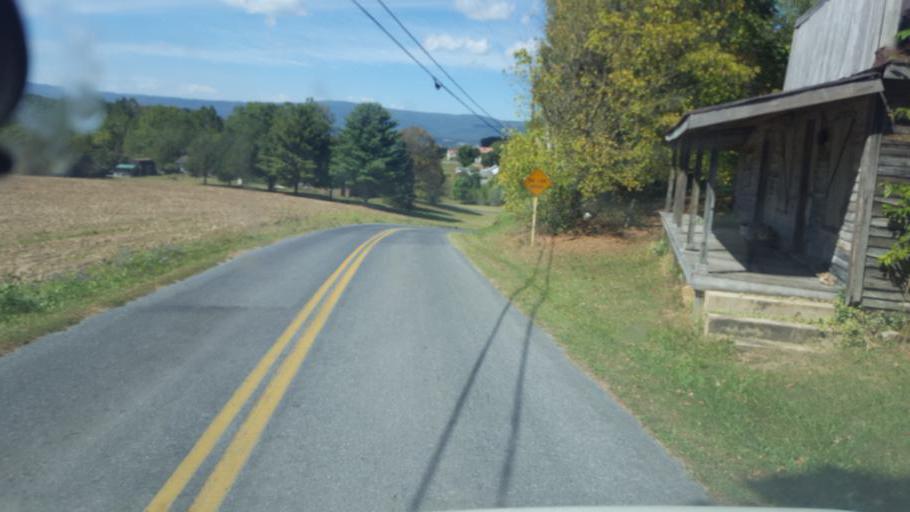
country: US
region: Virginia
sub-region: Rockingham County
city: Elkton
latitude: 38.3963
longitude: -78.5822
